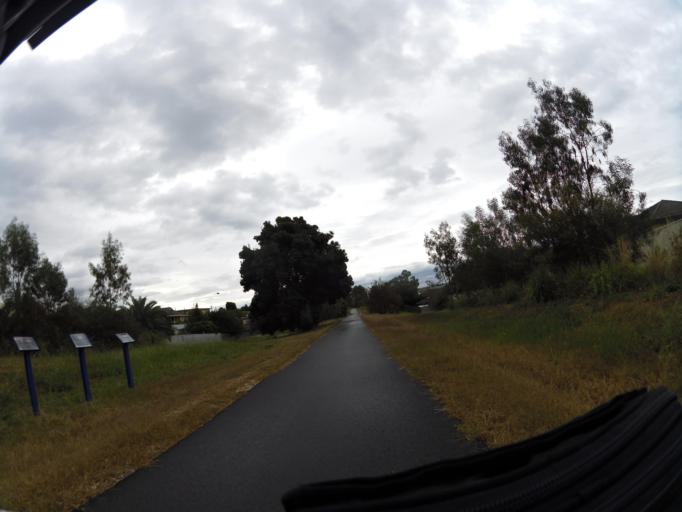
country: AU
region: Victoria
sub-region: Wodonga
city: Wodonga
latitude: -36.1269
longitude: 146.8949
